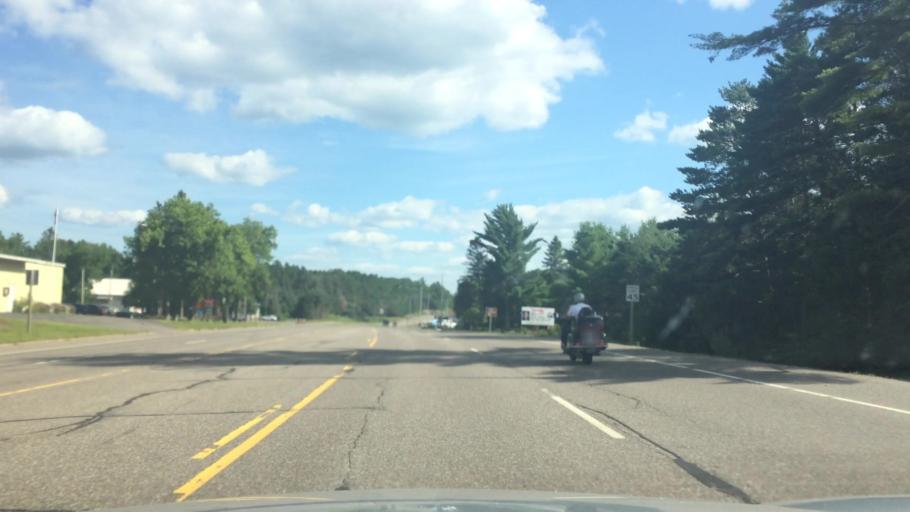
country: US
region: Wisconsin
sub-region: Vilas County
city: Lac du Flambeau
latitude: 45.8078
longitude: -89.7250
